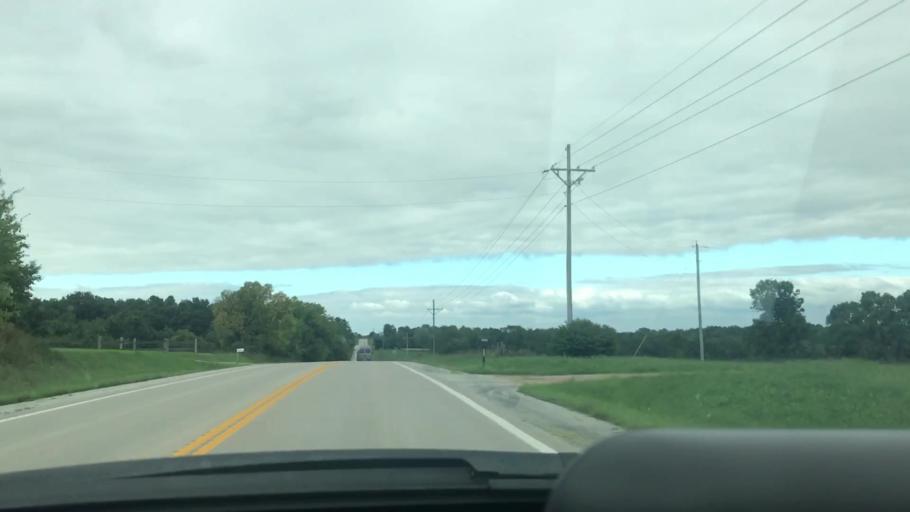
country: US
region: Missouri
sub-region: Hickory County
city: Hermitage
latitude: 37.8738
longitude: -93.1806
